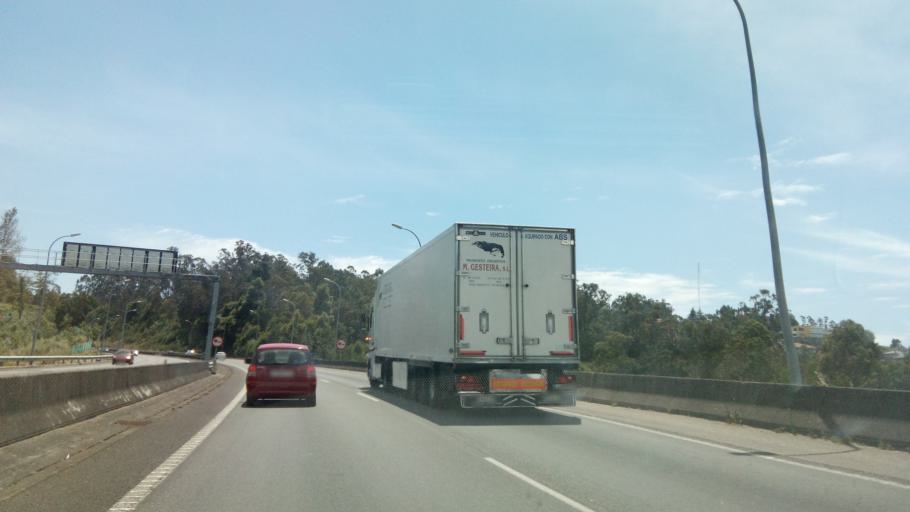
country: ES
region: Galicia
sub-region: Provincia de Pontevedra
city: Vigo
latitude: 42.2463
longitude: -8.6827
